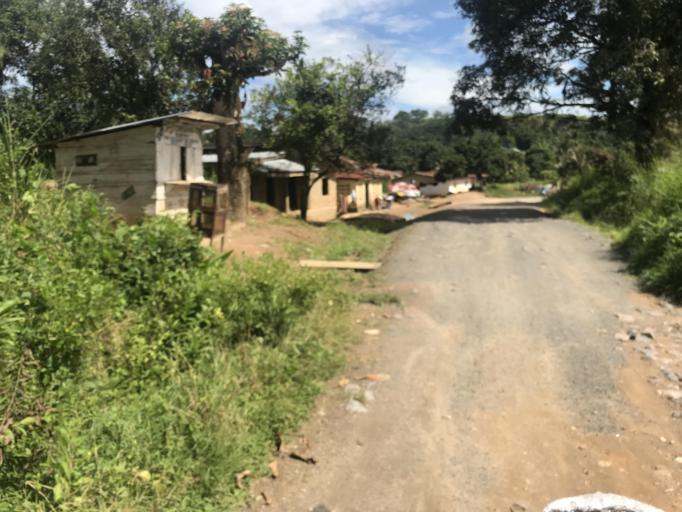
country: SL
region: Eastern Province
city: Koidu
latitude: 8.6430
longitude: -10.9878
